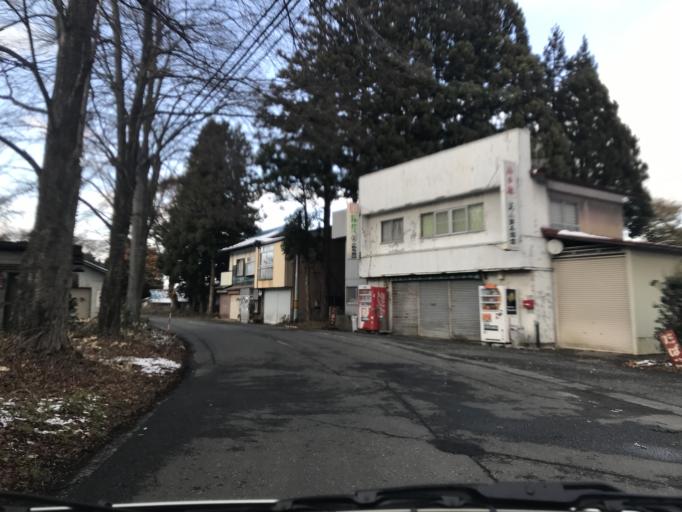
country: JP
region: Iwate
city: Kitakami
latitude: 39.2107
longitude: 141.0501
